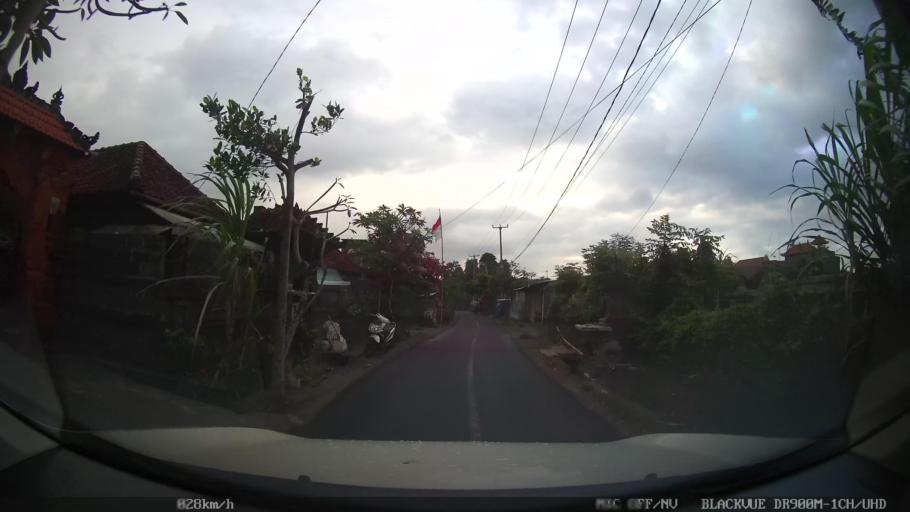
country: ID
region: Bali
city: Banjar Pasekan
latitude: -8.6256
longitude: 115.2785
